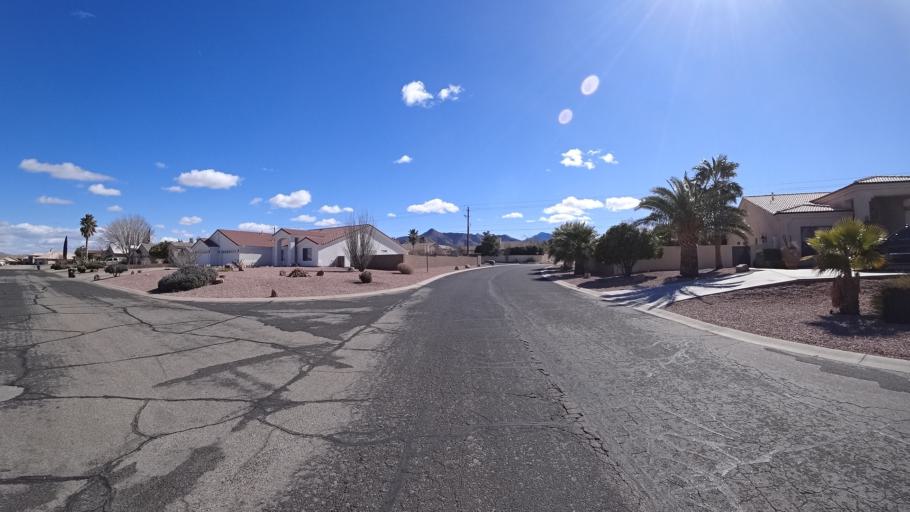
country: US
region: Arizona
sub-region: Mohave County
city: Kingman
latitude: 35.2034
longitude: -113.9739
